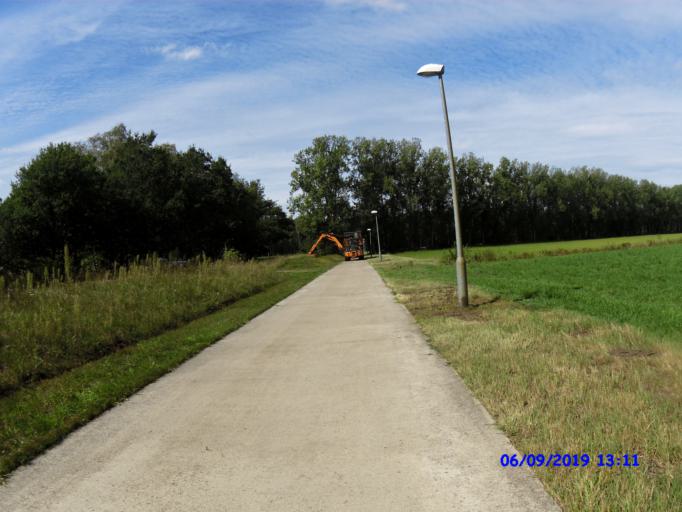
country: BE
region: Flanders
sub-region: Provincie Antwerpen
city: Geel
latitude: 51.2059
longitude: 5.0460
